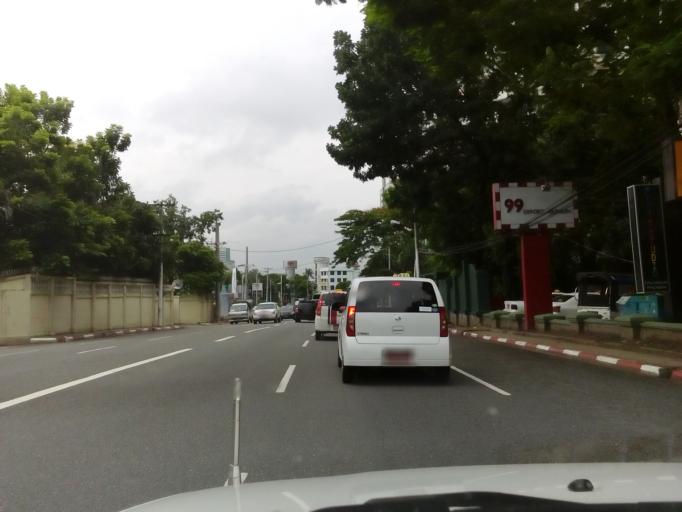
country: MM
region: Yangon
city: Yangon
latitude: 16.8161
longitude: 96.1561
